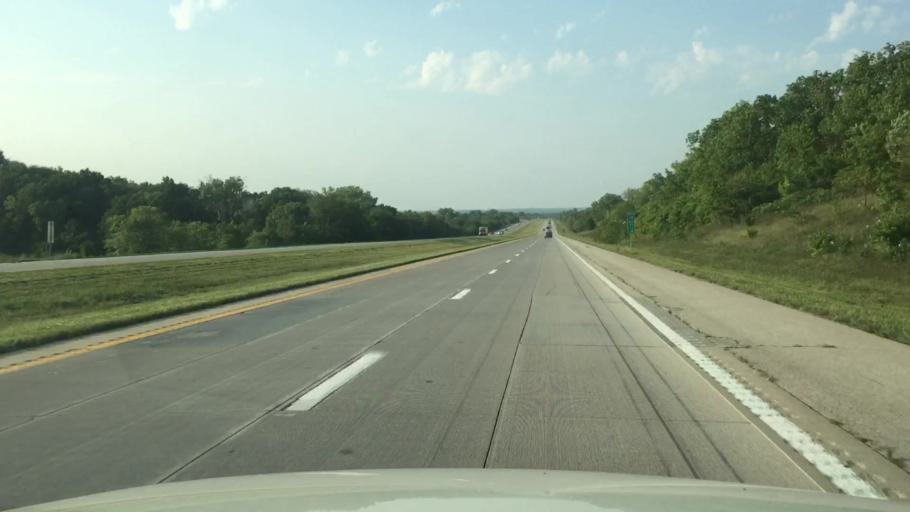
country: US
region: Missouri
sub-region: Daviess County
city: Gallatin
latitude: 39.9799
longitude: -94.0943
